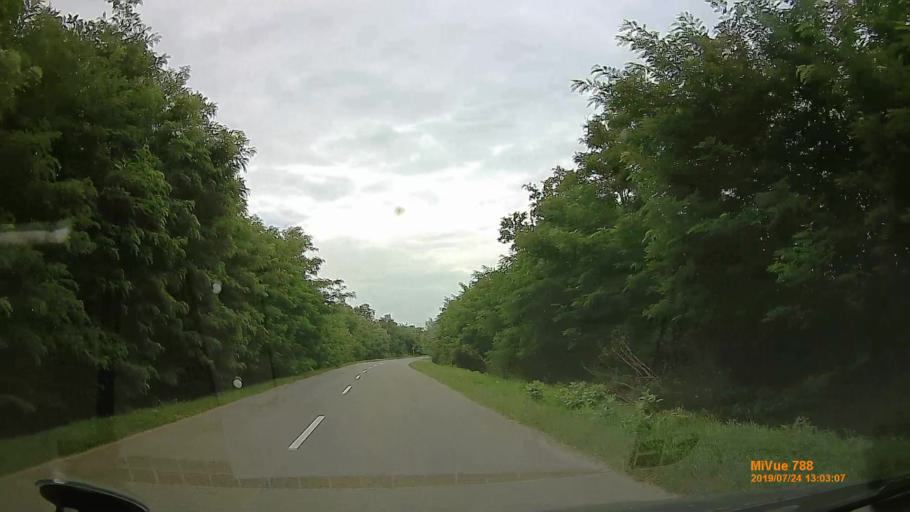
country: HU
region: Szabolcs-Szatmar-Bereg
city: Aranyosapati
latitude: 48.2162
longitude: 22.2985
